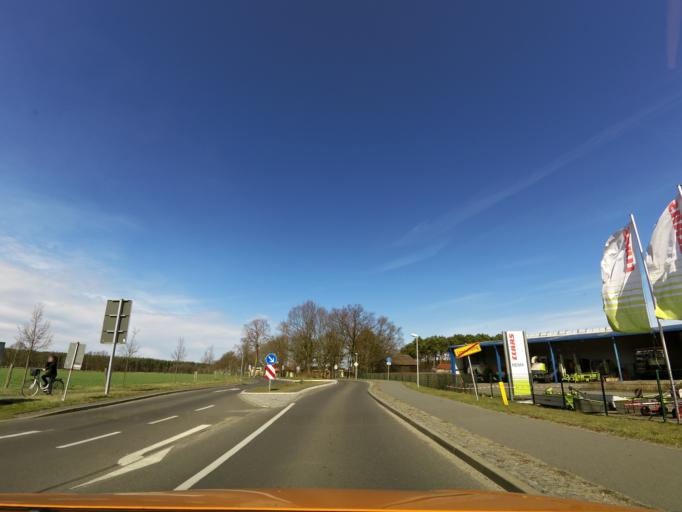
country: DE
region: Brandenburg
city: Belzig
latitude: 52.1799
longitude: 12.6242
